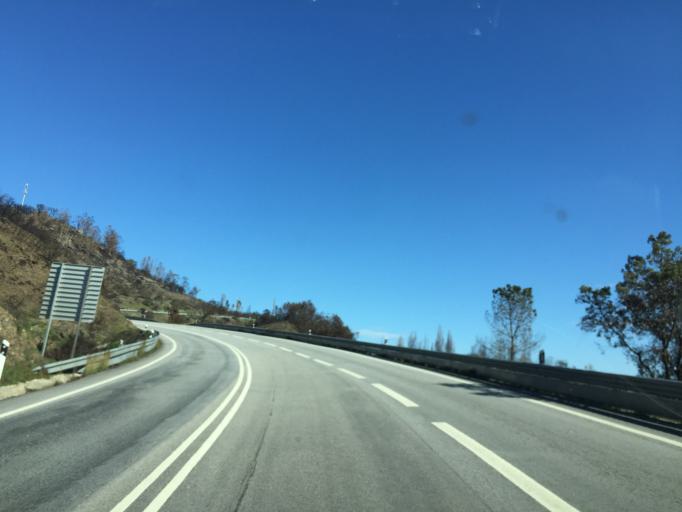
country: PT
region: Portalegre
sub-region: Nisa
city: Nisa
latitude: 39.5465
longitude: -7.7984
